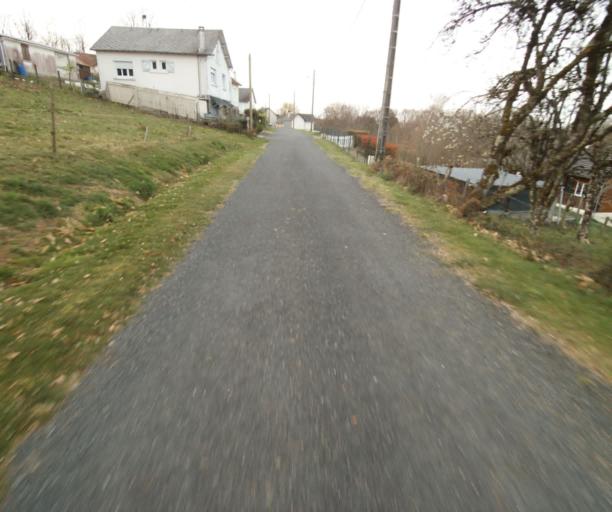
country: FR
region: Limousin
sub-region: Departement de la Correze
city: Correze
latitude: 45.4289
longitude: 1.8321
